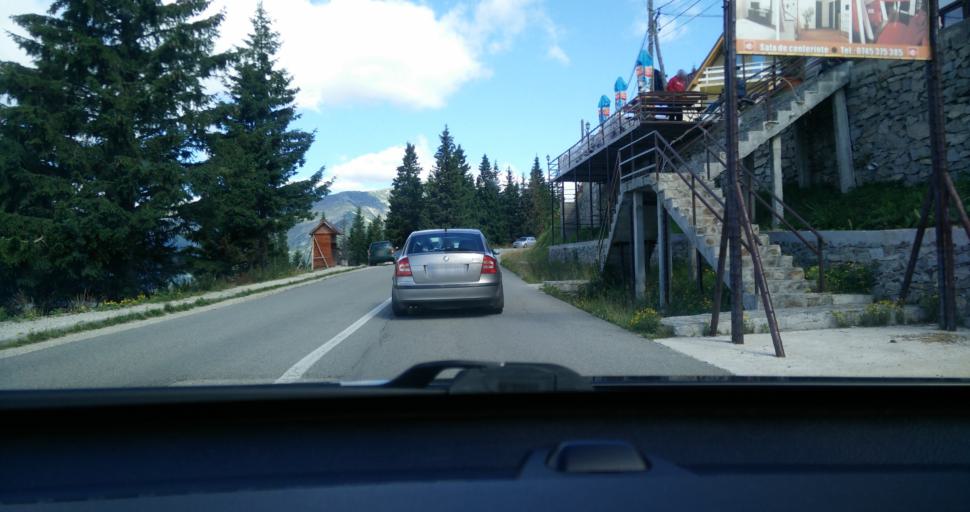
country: RO
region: Gorj
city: Novaci-Straini
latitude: 45.2981
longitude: 23.6810
